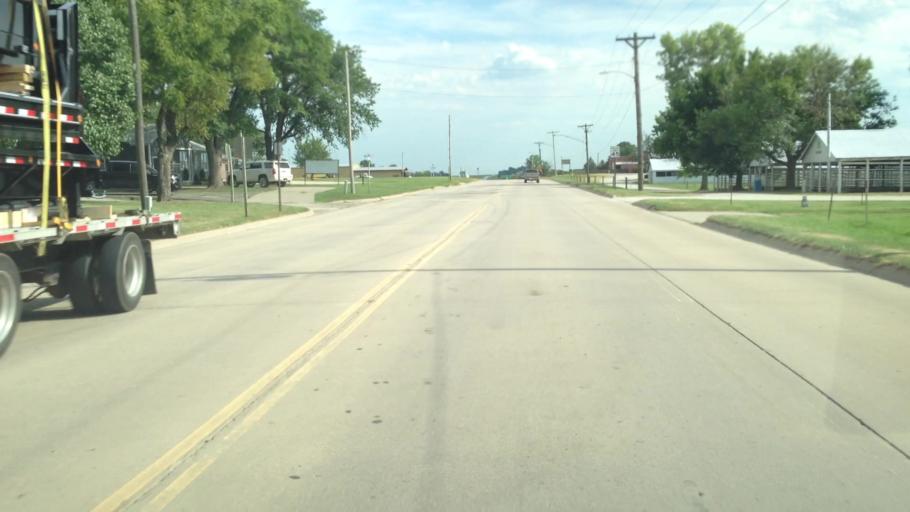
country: US
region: Kansas
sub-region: Woodson County
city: Yates Center
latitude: 37.8757
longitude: -95.7389
